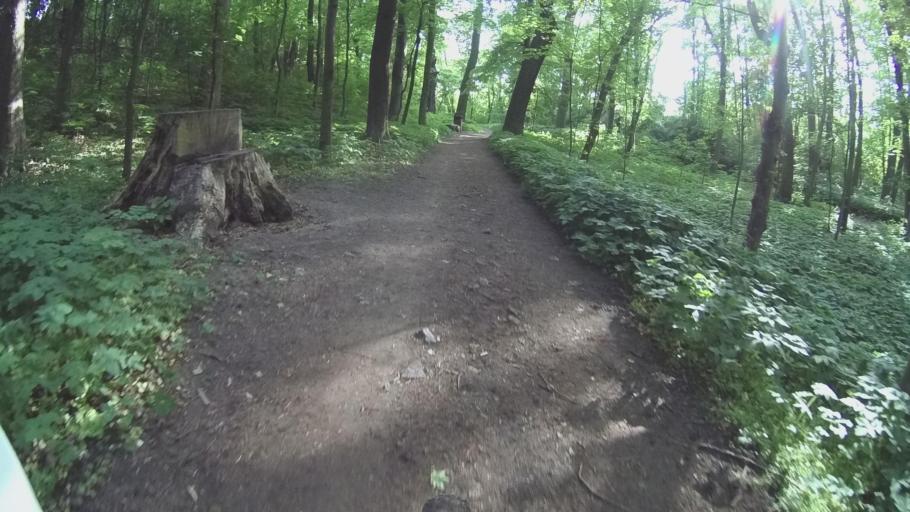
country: CZ
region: Praha
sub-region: Praha 19
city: Kbely
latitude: 50.1613
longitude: 14.5449
